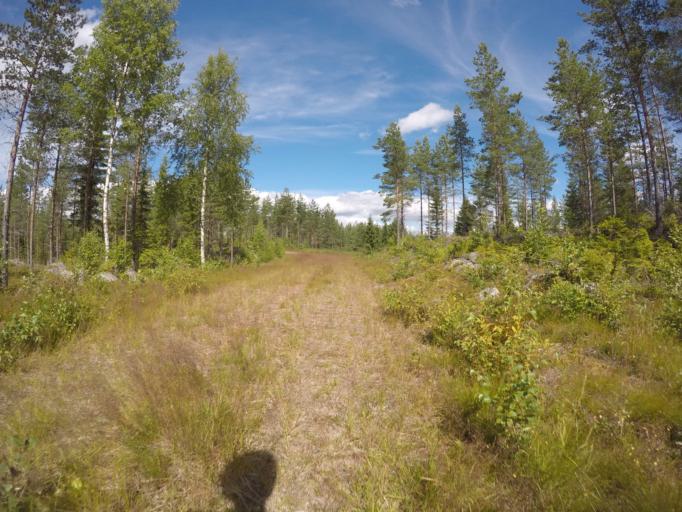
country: SE
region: OErebro
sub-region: Hallefors Kommun
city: Haellefors
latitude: 60.0847
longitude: 14.4913
